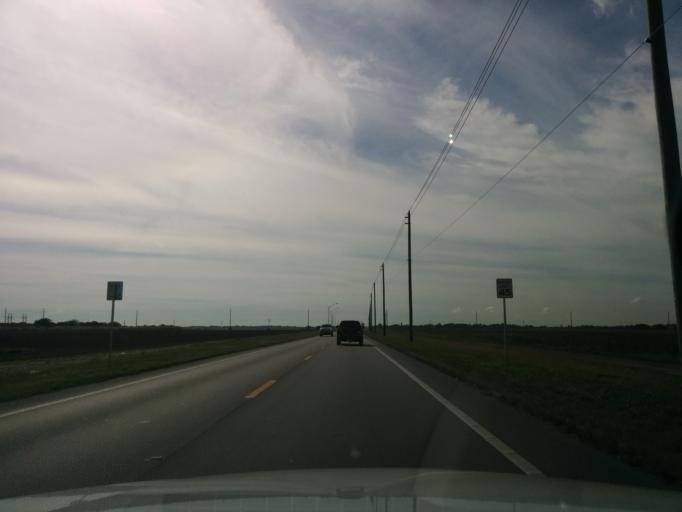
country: US
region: Florida
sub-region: Miami-Dade County
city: The Hammocks
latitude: 25.6448
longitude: -80.4802
